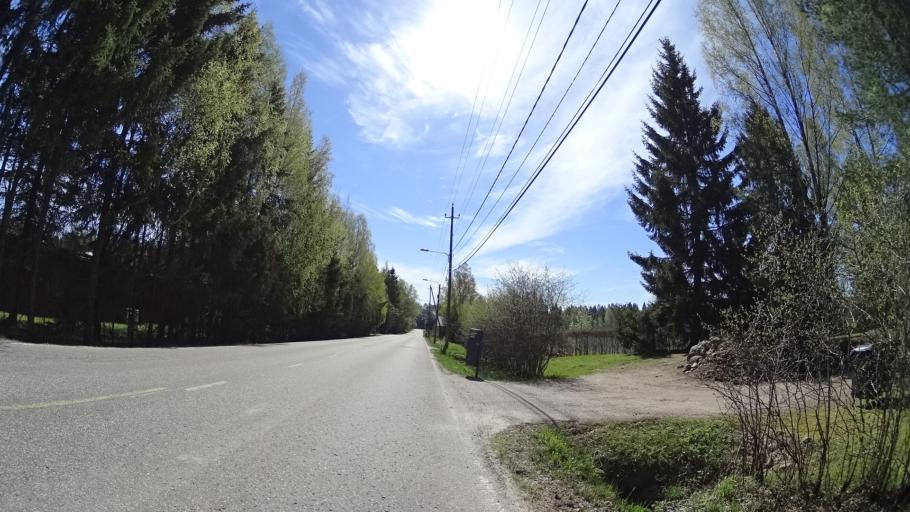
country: FI
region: Uusimaa
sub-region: Helsinki
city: Nurmijaervi
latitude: 60.3683
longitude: 24.8418
